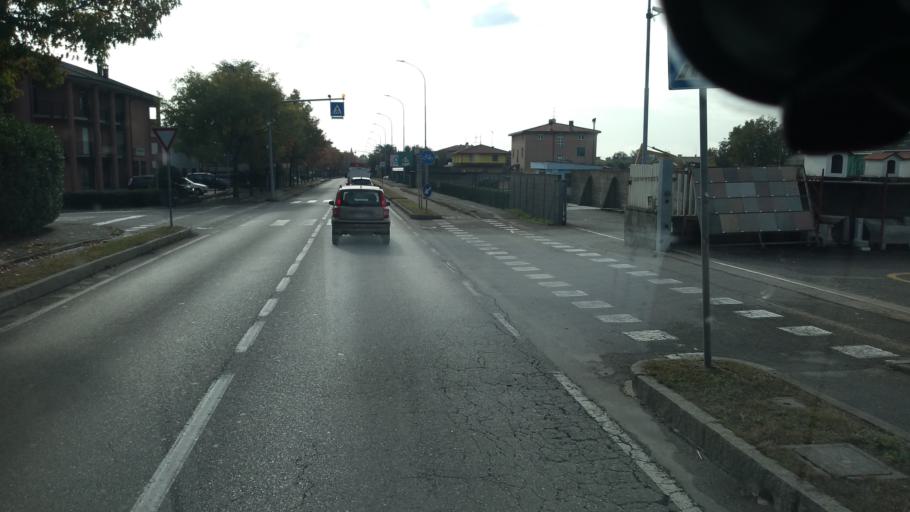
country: IT
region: Lombardy
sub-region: Provincia di Bergamo
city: Cologno al Serio
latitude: 45.5879
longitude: 9.7033
